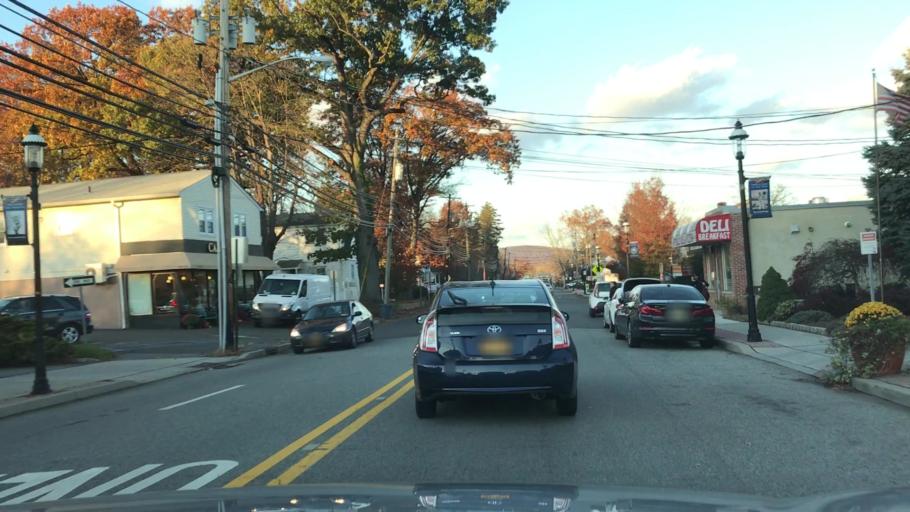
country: US
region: New Jersey
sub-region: Bergen County
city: Northvale
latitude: 41.0073
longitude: -73.9488
